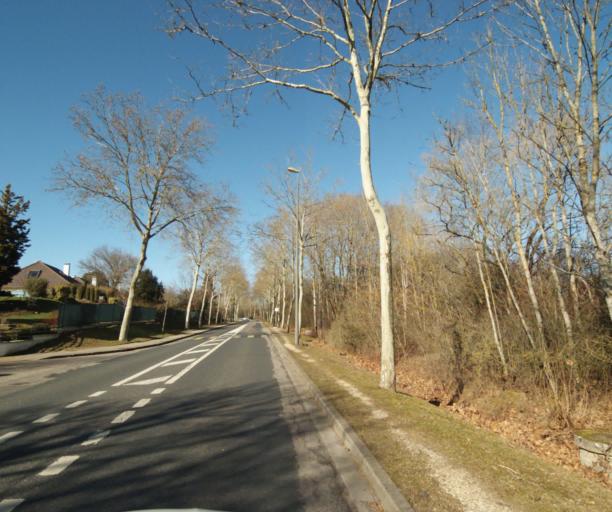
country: FR
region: Lorraine
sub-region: Departement de Meurthe-et-Moselle
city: Heillecourt
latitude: 48.6533
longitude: 6.2030
